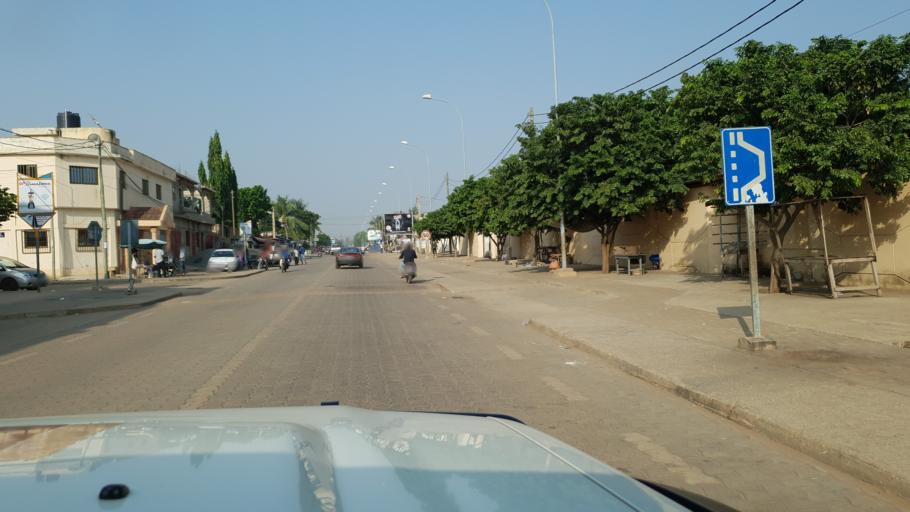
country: TG
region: Maritime
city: Lome
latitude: 6.1823
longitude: 1.2023
